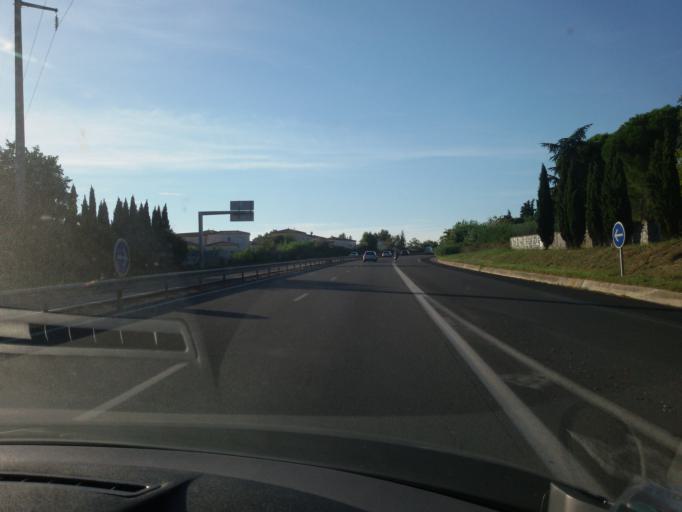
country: FR
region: Languedoc-Roussillon
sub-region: Departement de l'Herault
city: Juvignac
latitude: 43.6115
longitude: 3.8020
